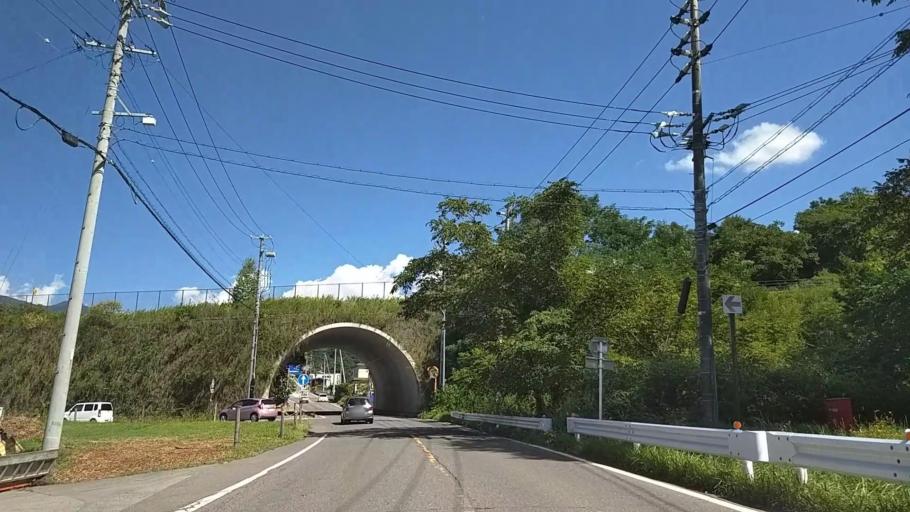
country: JP
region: Nagano
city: Chino
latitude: 36.0324
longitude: 138.2214
